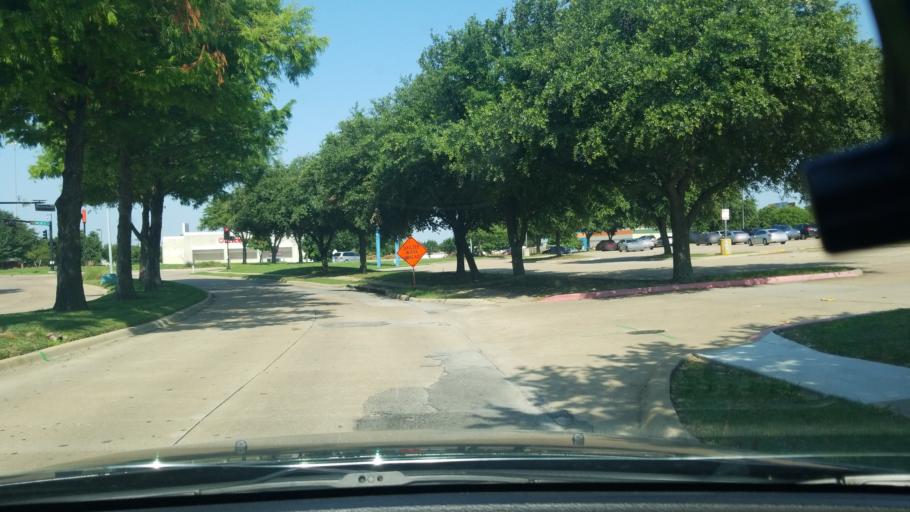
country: US
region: Texas
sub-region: Dallas County
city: Mesquite
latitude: 32.8150
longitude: -96.6250
